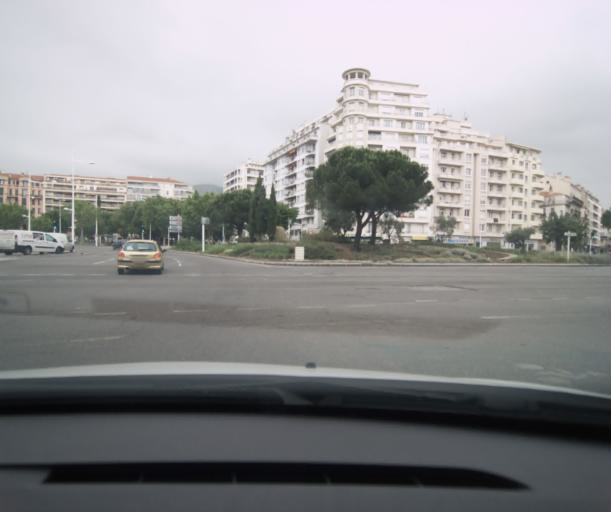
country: FR
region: Provence-Alpes-Cote d'Azur
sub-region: Departement du Var
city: Toulon
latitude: 43.1212
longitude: 5.9407
